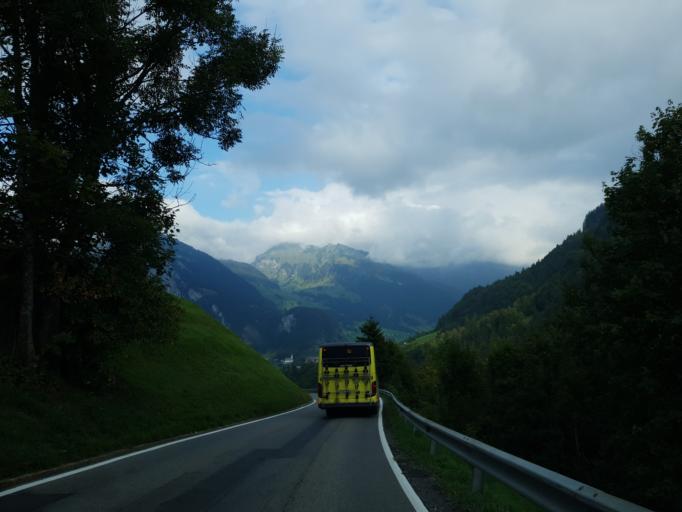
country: AT
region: Vorarlberg
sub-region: Politischer Bezirk Bregenz
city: Au
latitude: 47.3107
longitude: 9.9487
